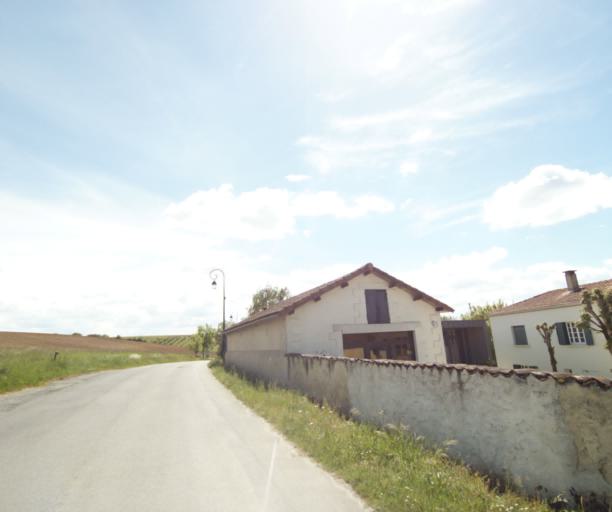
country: FR
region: Poitou-Charentes
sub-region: Departement de la Charente-Maritime
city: Chaniers
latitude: 45.7342
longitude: -0.5075
